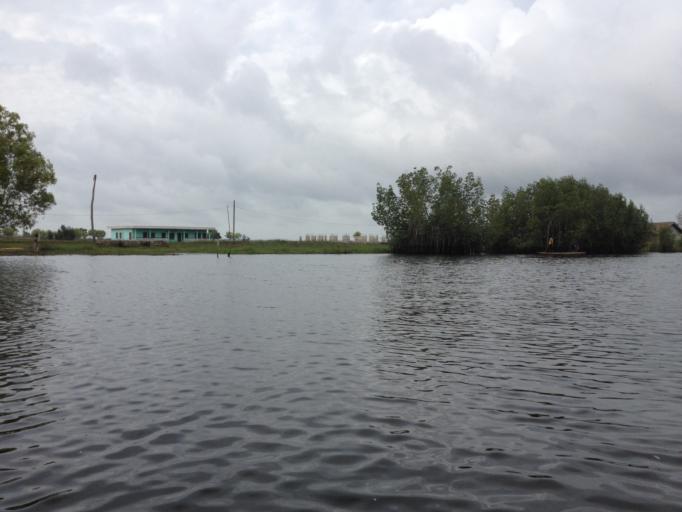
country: BJ
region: Mono
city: Come
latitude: 6.3817
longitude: 1.9379
